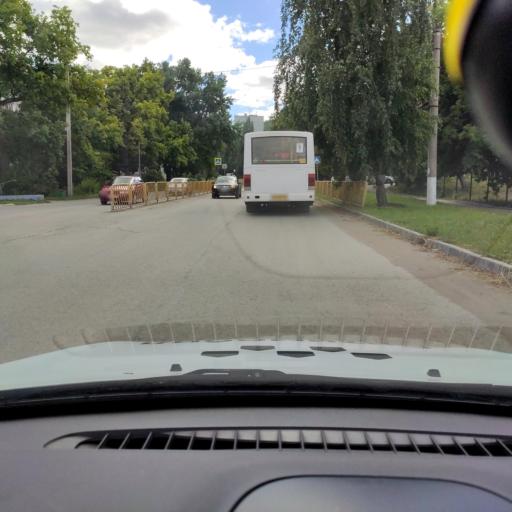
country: RU
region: Samara
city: Zhigulevsk
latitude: 53.4063
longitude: 49.4066
